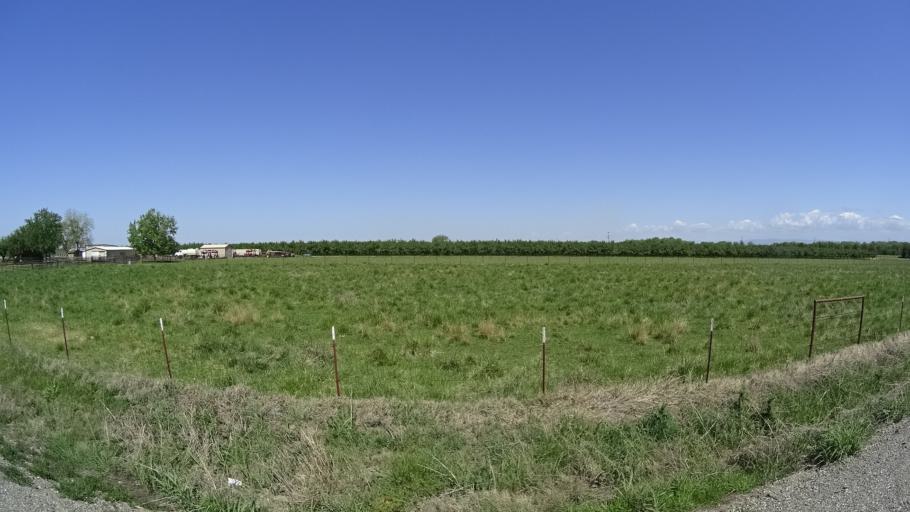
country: US
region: California
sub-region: Glenn County
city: Hamilton City
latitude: 39.7664
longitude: -122.0366
